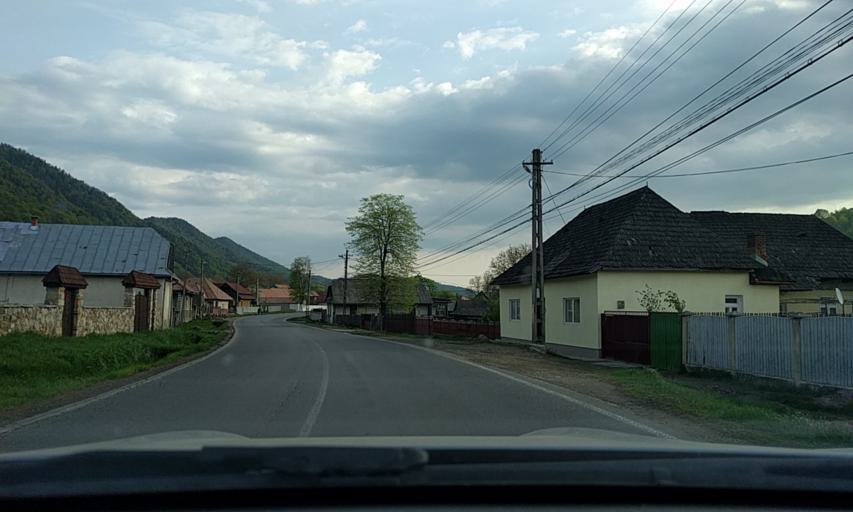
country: RO
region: Bacau
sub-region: Oras Slanic-Moldova
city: Slanic-Moldova
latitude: 46.1452
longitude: 26.4572
